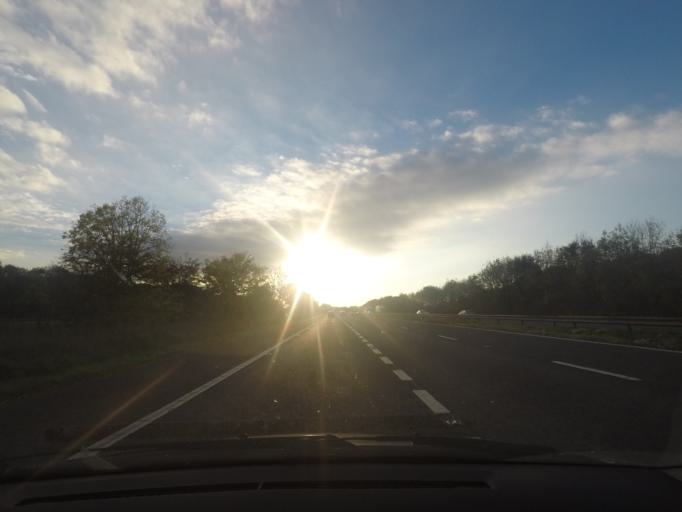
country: GB
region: England
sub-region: North Lincolnshire
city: Scawby
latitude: 53.5474
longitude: -0.5352
